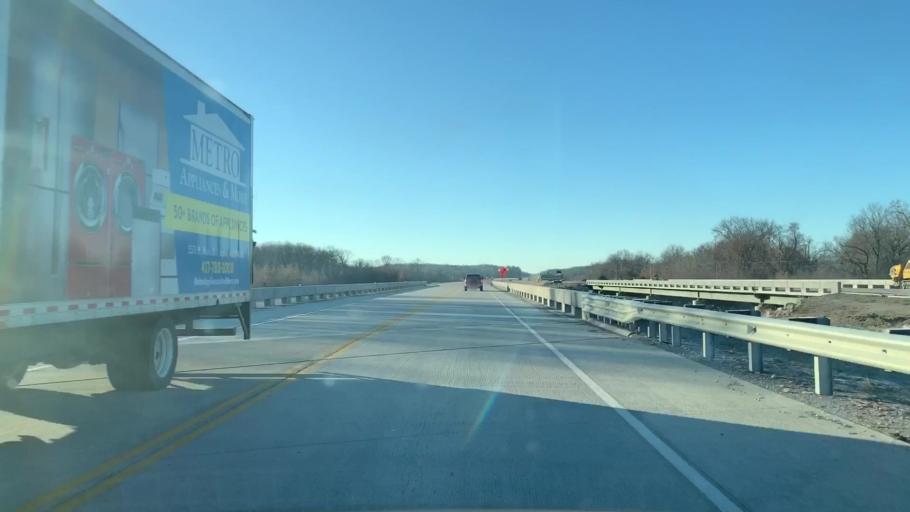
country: US
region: Kansas
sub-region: Crawford County
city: Arma
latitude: 37.6818
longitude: -94.7034
